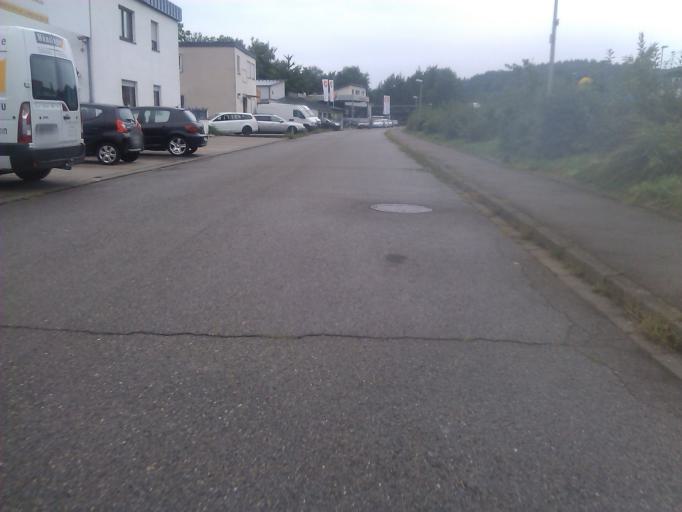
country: DE
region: Baden-Wuerttemberg
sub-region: Regierungsbezirk Stuttgart
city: Neckartenzlingen
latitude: 48.5882
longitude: 9.2298
